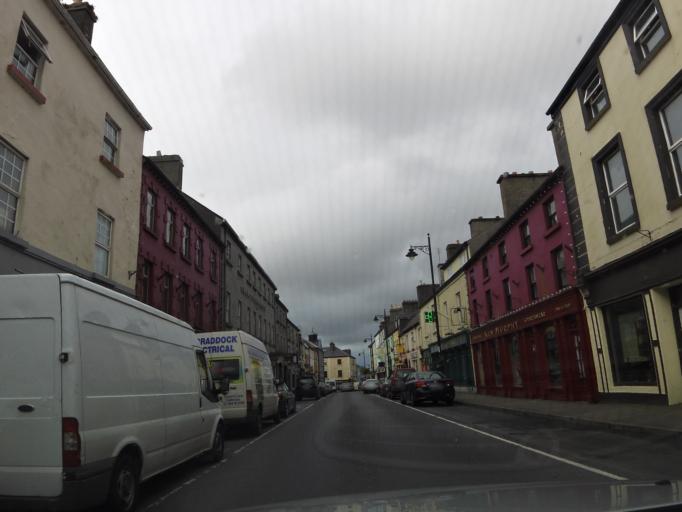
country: IE
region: Connaught
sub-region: Maigh Eo
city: Ballinrobe
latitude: 53.6229
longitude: -9.2228
